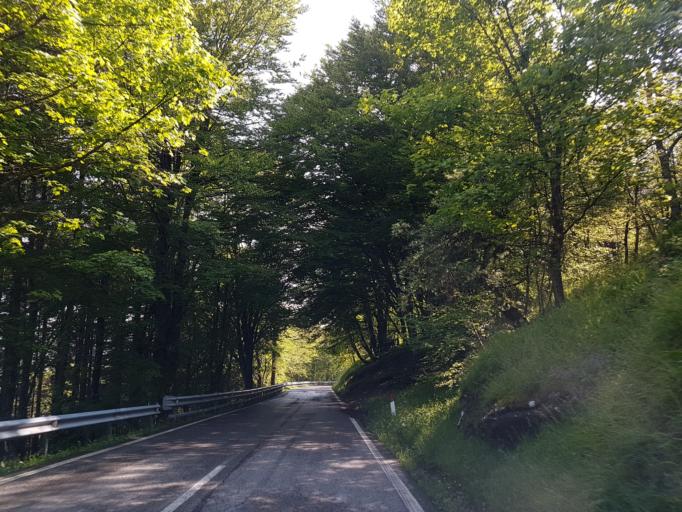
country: IT
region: Emilia-Romagna
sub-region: Forli-Cesena
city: San Piero in Bagno
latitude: 43.7956
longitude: 11.8975
